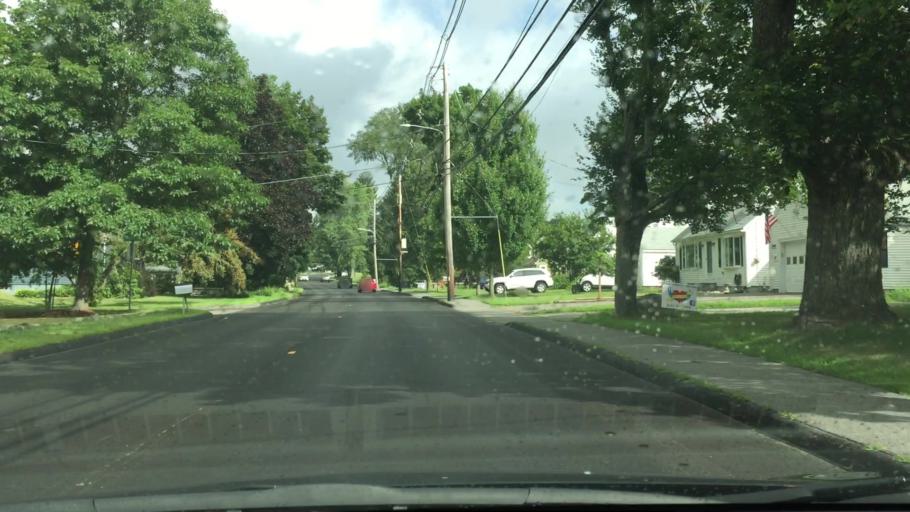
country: US
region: Massachusetts
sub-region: Middlesex County
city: Littleton Common
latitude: 42.5380
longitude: -71.4670
